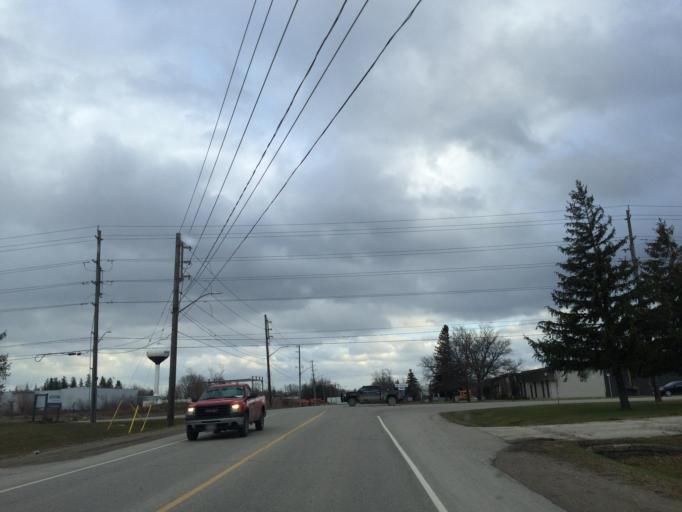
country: CA
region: Ontario
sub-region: Wellington County
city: Guelph
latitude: 43.5411
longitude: -80.3024
